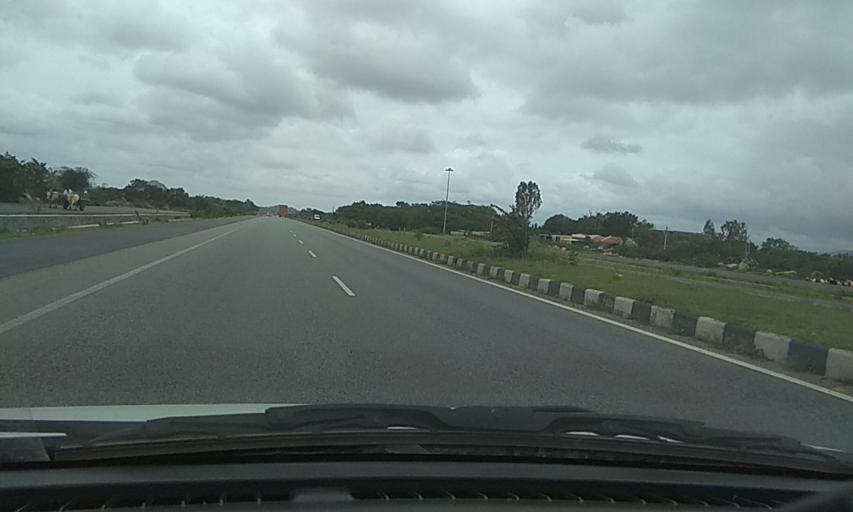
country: IN
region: Karnataka
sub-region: Chitradurga
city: Chitradurga
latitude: 14.2706
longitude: 76.3283
